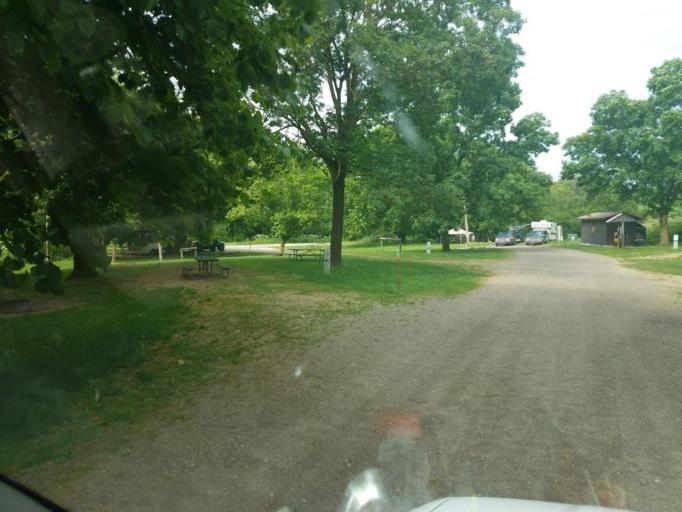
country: US
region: Wisconsin
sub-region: Monroe County
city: Cashton
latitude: 43.7114
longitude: -90.5629
